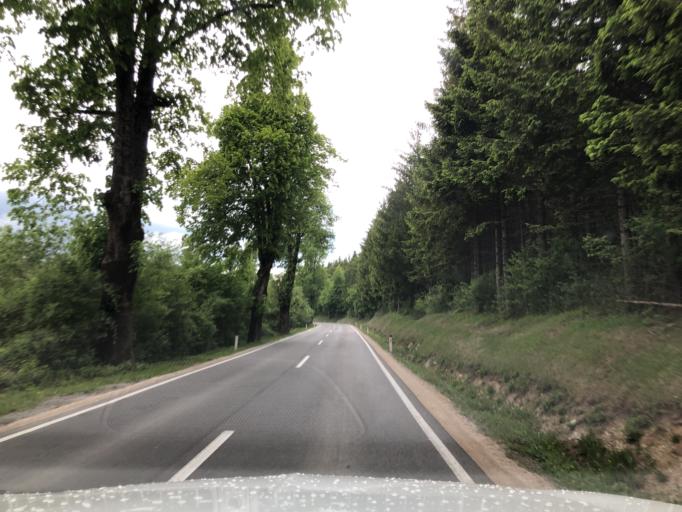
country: SI
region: Cerknica
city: Rakek
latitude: 45.7991
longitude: 14.3335
